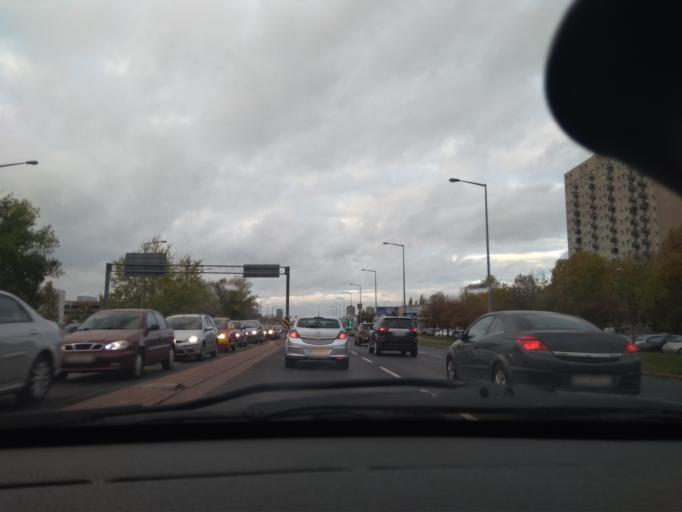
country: PL
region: Greater Poland Voivodeship
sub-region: Poznan
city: Poznan
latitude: 52.4363
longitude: 16.9210
